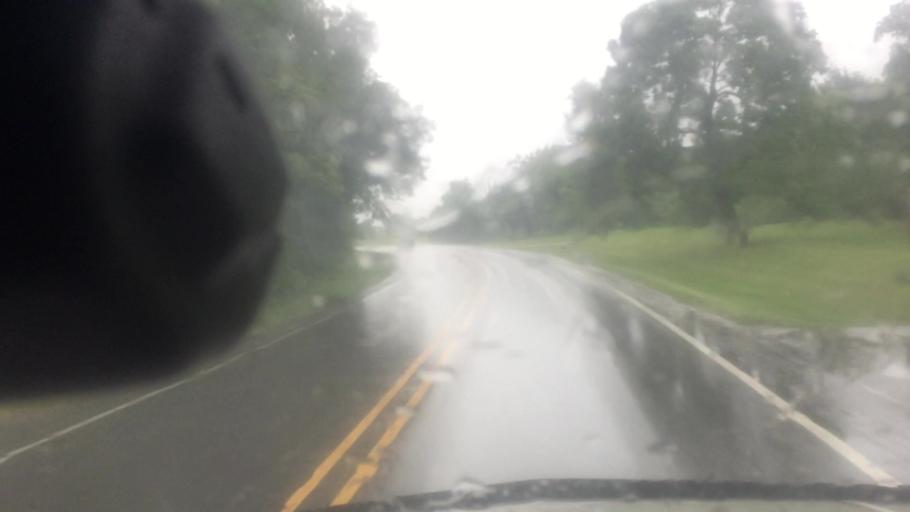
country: US
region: Illinois
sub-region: Madison County
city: Edwardsville
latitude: 38.8328
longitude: -89.9182
